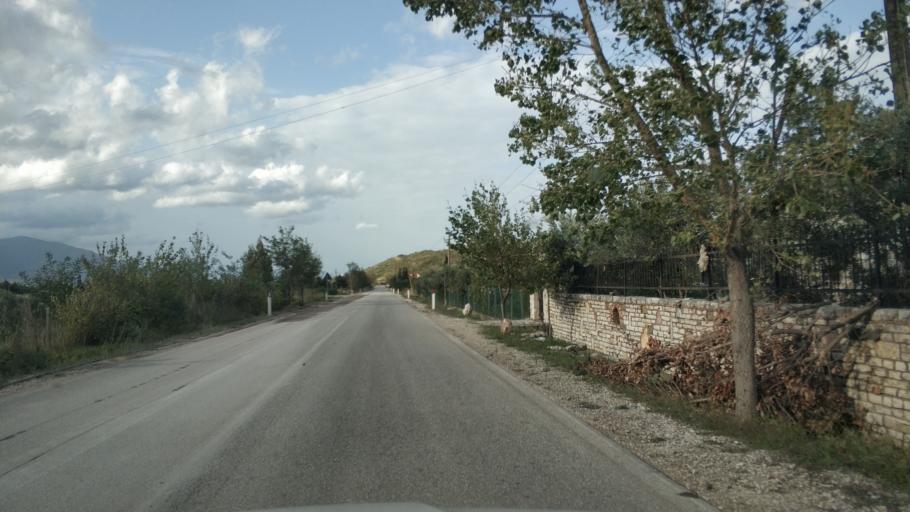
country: AL
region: Vlore
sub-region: Rrethi i Vlores
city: Orikum
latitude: 40.2890
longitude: 19.4933
